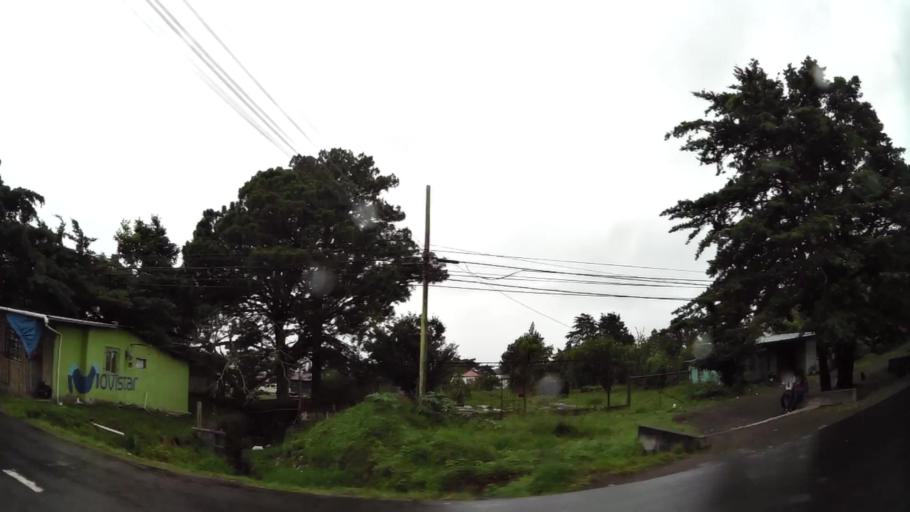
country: PA
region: Chiriqui
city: Volcan
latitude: 8.7766
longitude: -82.6401
